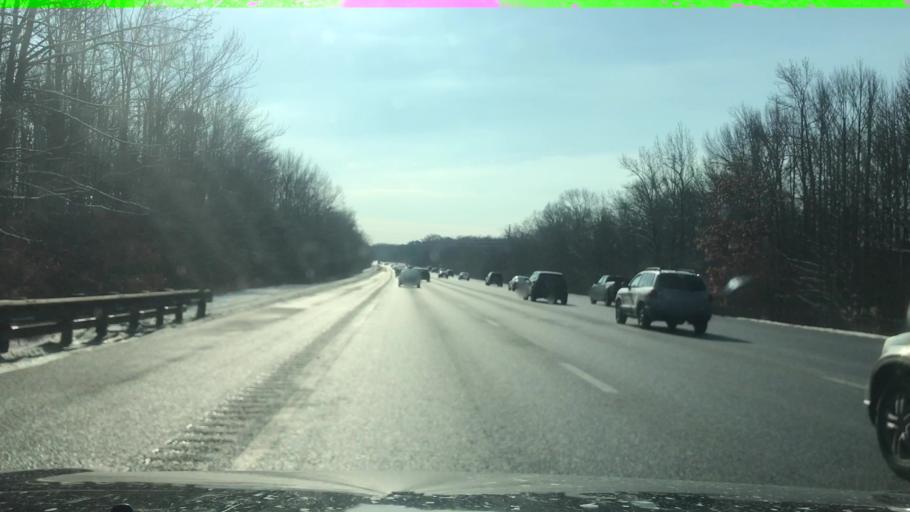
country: US
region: New Jersey
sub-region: Monmouth County
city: Shark River Hills
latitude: 40.1896
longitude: -74.1009
